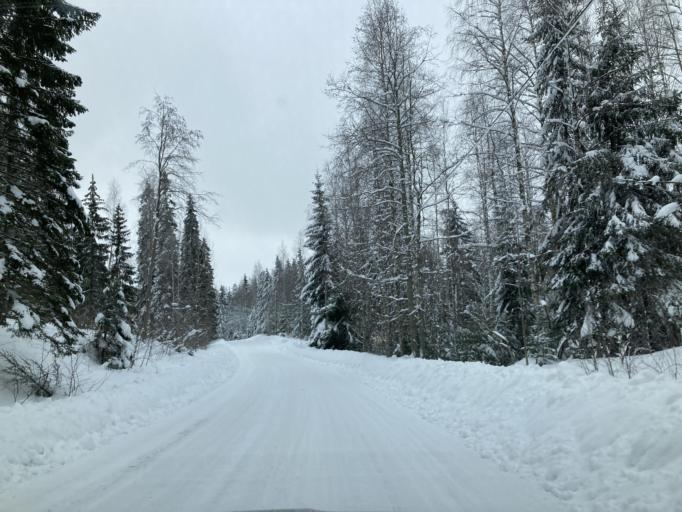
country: FI
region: Central Finland
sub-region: Jaemsae
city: Jaemsae
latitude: 61.8787
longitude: 25.3202
